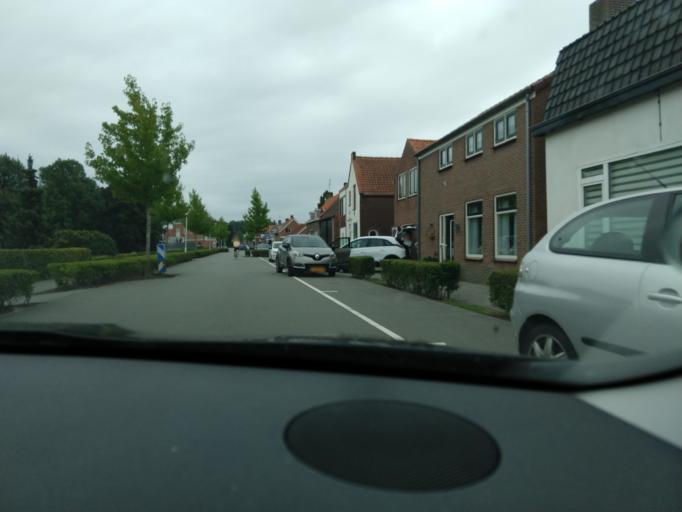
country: NL
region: Zeeland
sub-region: Gemeente Hulst
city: Hulst
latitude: 51.3173
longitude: 4.0344
